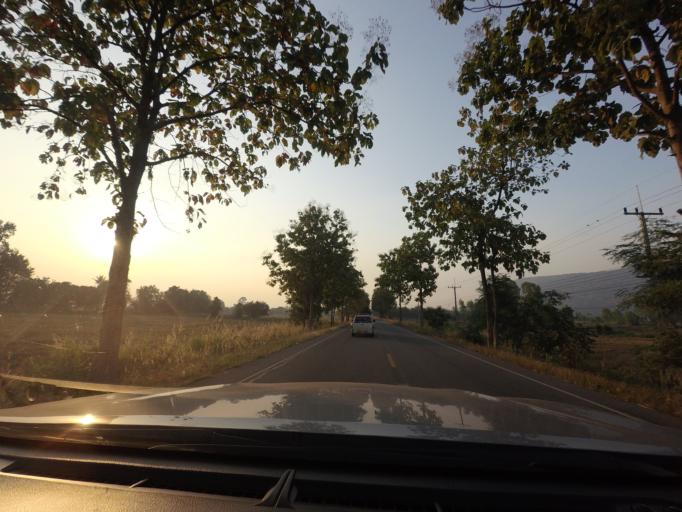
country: TH
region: Phitsanulok
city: Wang Thong
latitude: 16.7080
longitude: 100.4890
